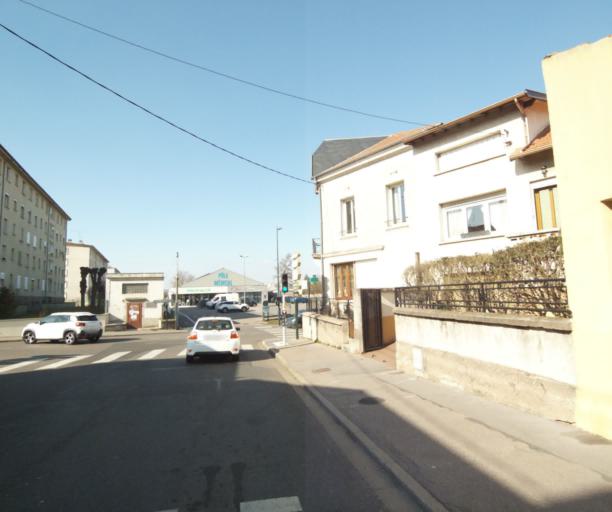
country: FR
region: Lorraine
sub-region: Departement de Meurthe-et-Moselle
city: Jarville-la-Malgrange
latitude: 48.6694
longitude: 6.2000
